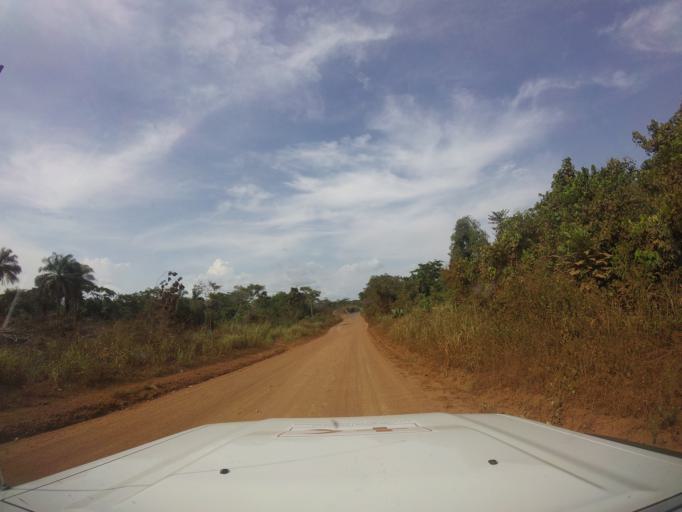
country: LR
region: Grand Cape Mount
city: Robertsport
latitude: 6.7184
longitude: -11.0832
